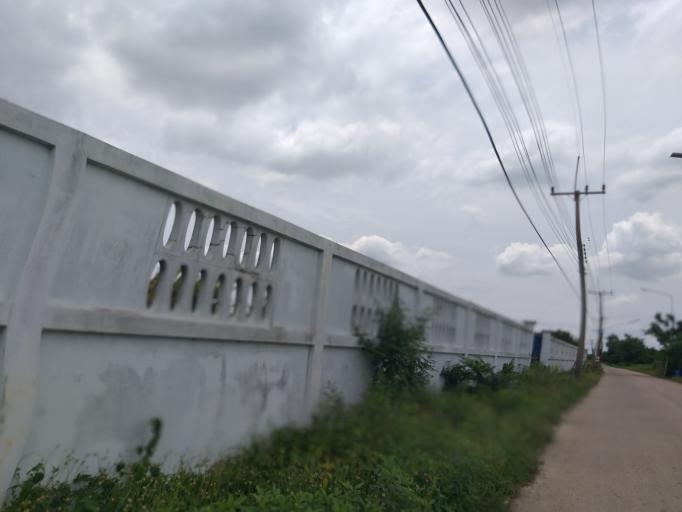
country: TH
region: Pathum Thani
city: Ban Lam Luk Ka
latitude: 13.9628
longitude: 100.8540
